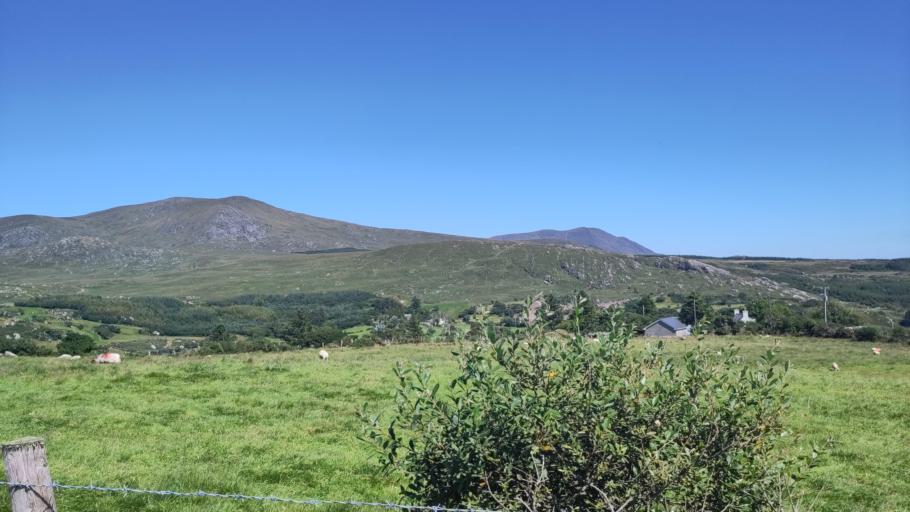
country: IE
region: Munster
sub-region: Ciarrai
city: Kenmare
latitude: 51.6656
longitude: -9.9101
